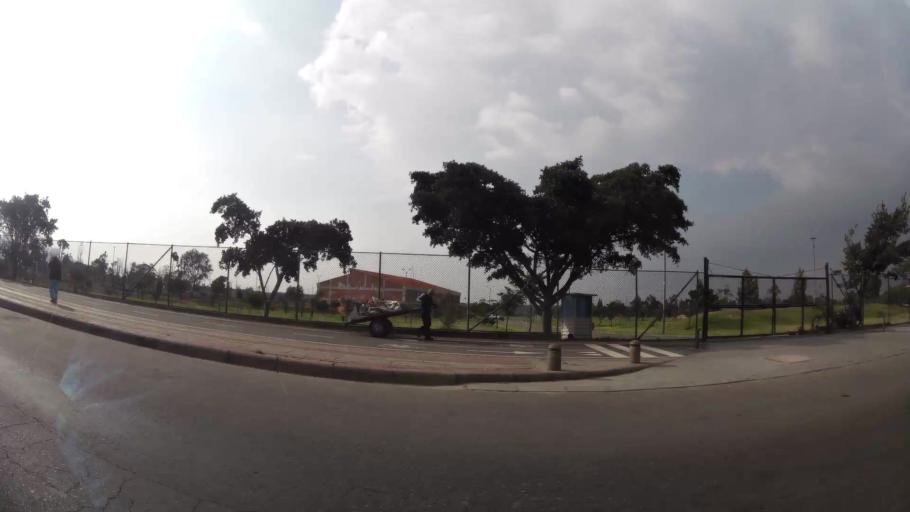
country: CO
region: Bogota D.C.
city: Bogota
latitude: 4.5699
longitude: -74.1321
